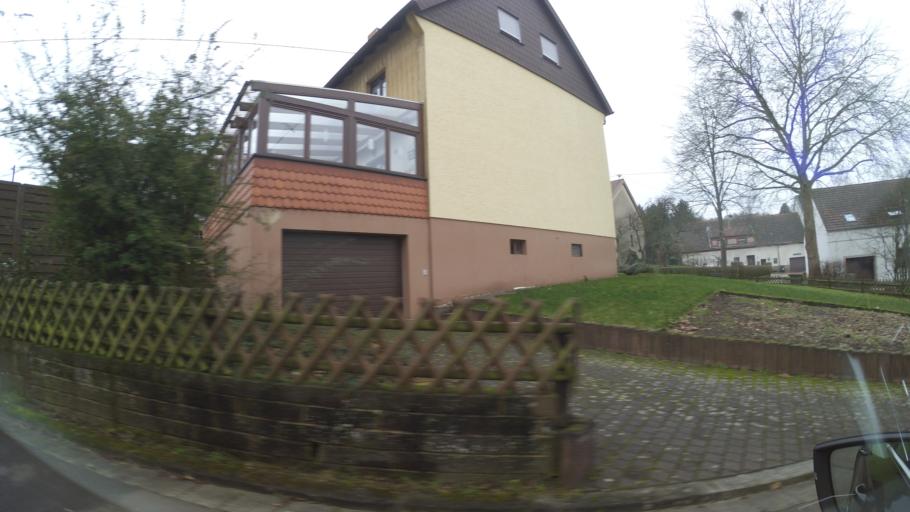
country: DE
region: Saarland
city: Mainzweiler
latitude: 49.3974
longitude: 7.0937
